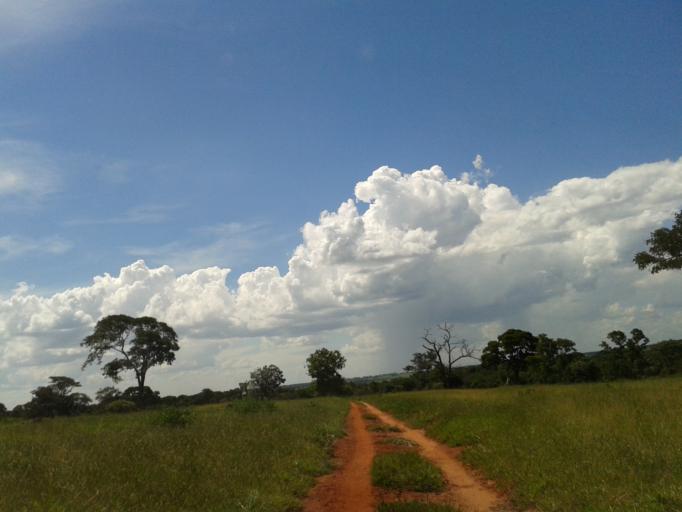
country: BR
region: Minas Gerais
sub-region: Santa Vitoria
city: Santa Vitoria
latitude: -19.1457
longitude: -50.5411
